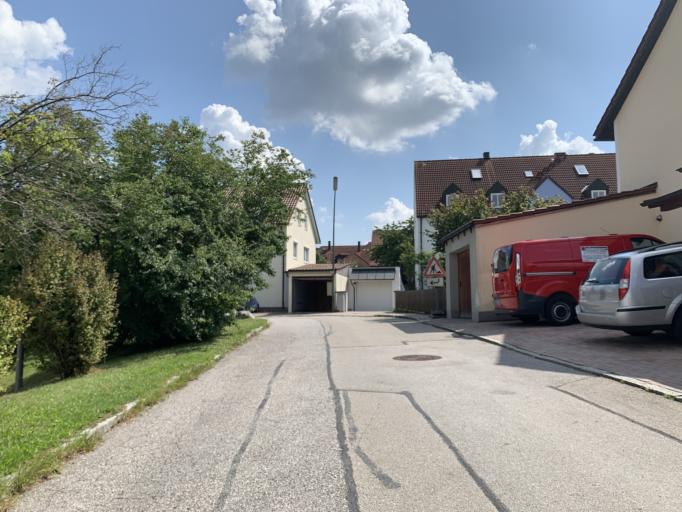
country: DE
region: Bavaria
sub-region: Upper Bavaria
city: Freising
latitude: 48.4102
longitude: 11.7392
